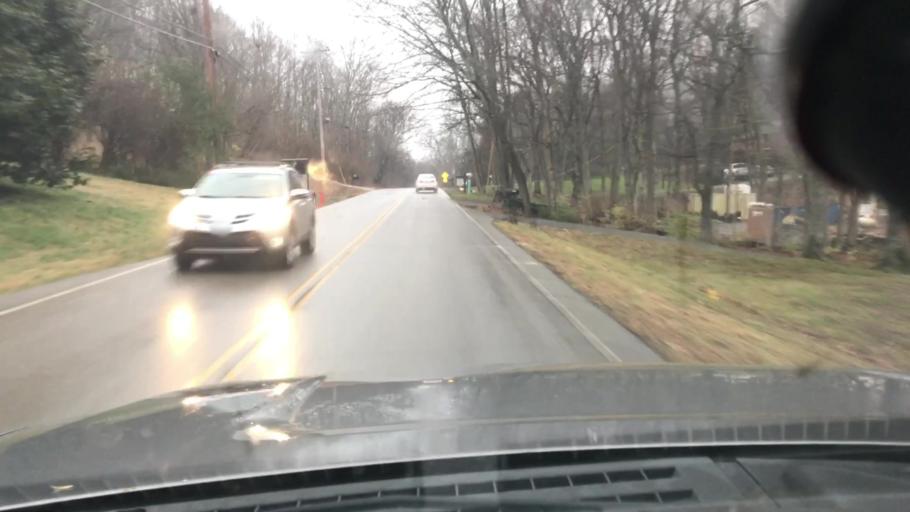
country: US
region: Tennessee
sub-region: Davidson County
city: Forest Hills
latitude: 36.0657
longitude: -86.8588
